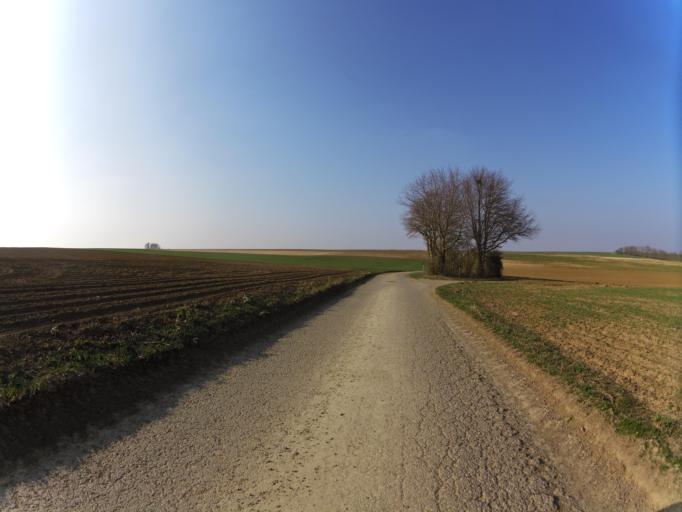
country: DE
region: Bavaria
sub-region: Regierungsbezirk Unterfranken
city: Winterhausen
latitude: 49.6890
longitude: 9.9839
